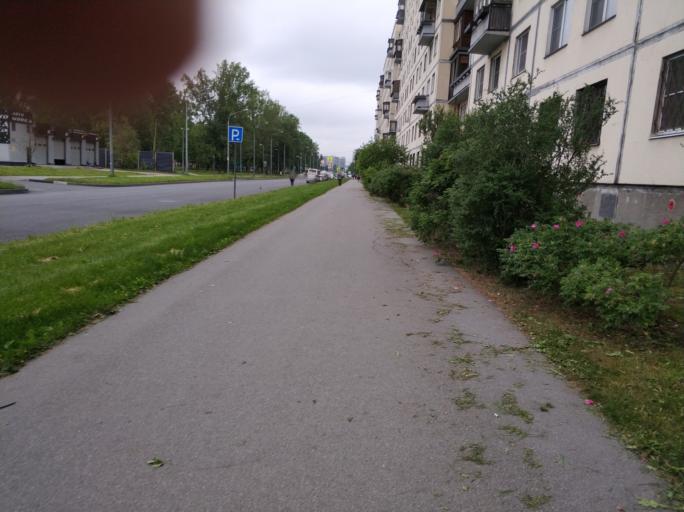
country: RU
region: St.-Petersburg
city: Grazhdanka
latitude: 60.0382
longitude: 30.4124
